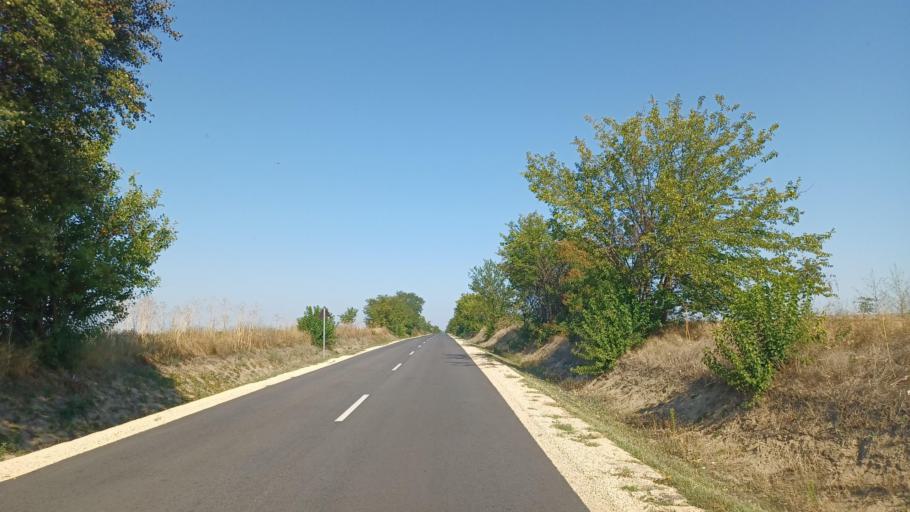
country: HU
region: Tolna
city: Paks
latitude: 46.6481
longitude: 18.8438
